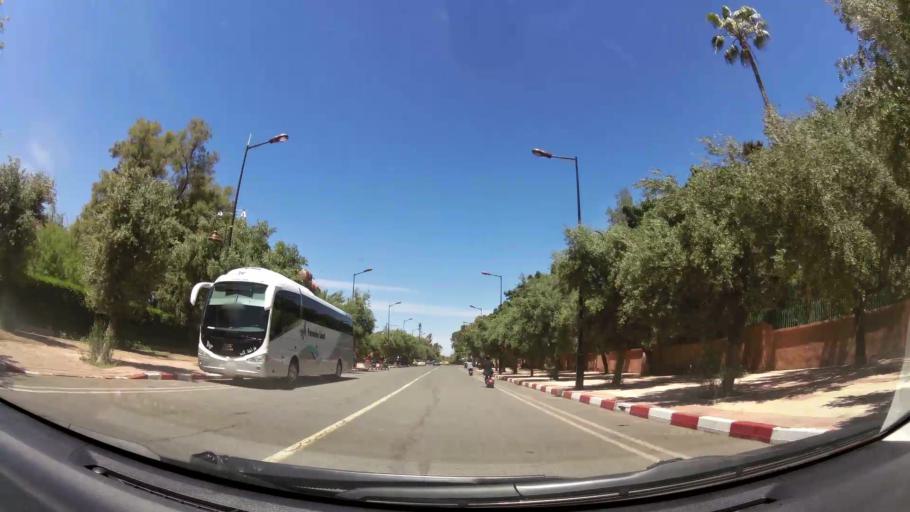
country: MA
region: Marrakech-Tensift-Al Haouz
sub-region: Marrakech
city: Marrakesh
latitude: 31.6201
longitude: -8.0061
